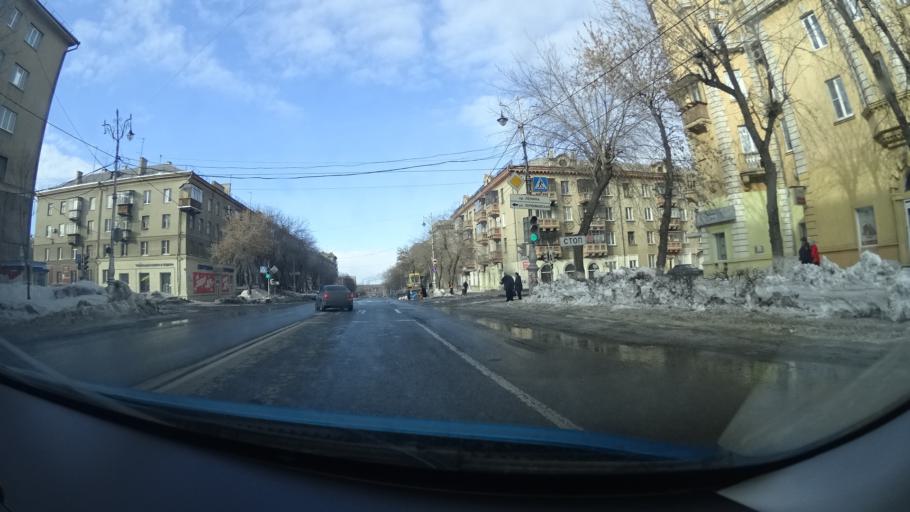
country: RU
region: Chelyabinsk
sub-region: Gorod Magnitogorsk
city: Magnitogorsk
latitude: 53.4316
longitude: 58.9837
